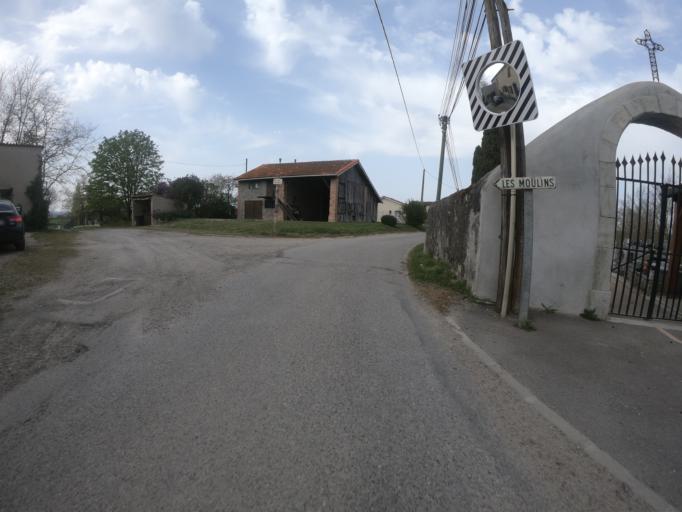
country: FR
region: Languedoc-Roussillon
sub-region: Departement de l'Aude
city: Belpech
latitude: 43.1459
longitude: 1.7139
